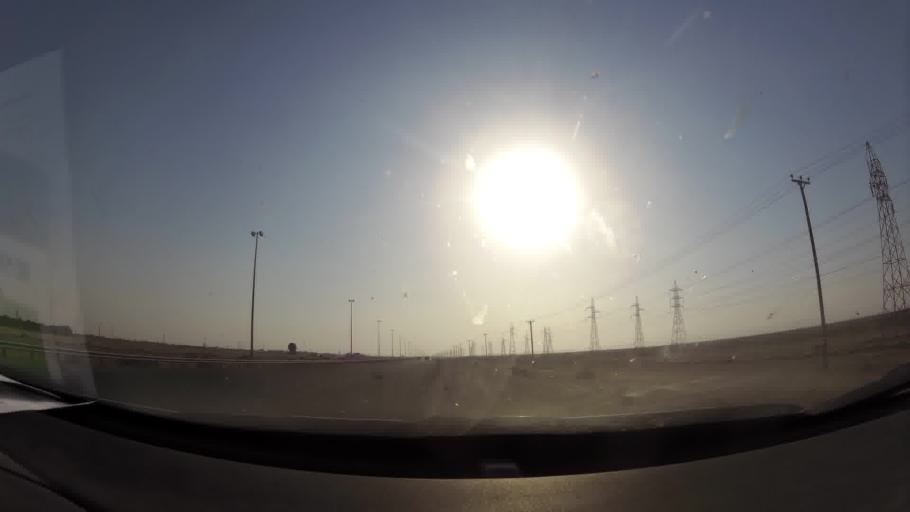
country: IQ
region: Basra Governorate
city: Umm Qasr
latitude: 30.0610
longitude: 47.6787
